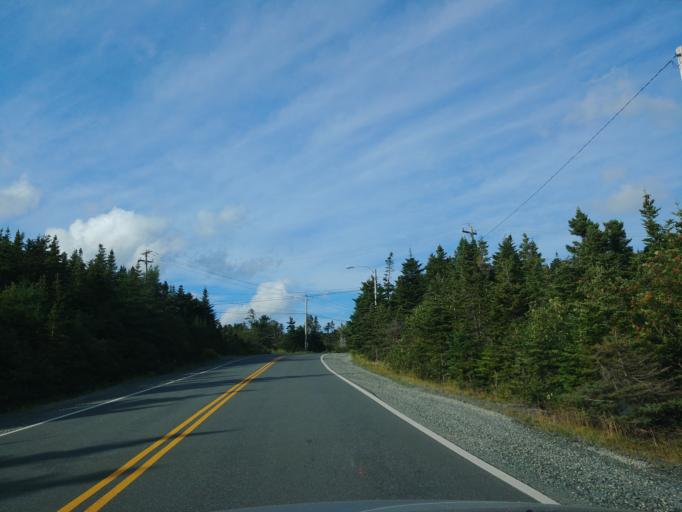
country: CA
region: Newfoundland and Labrador
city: St. John's
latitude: 47.5687
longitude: -52.7621
